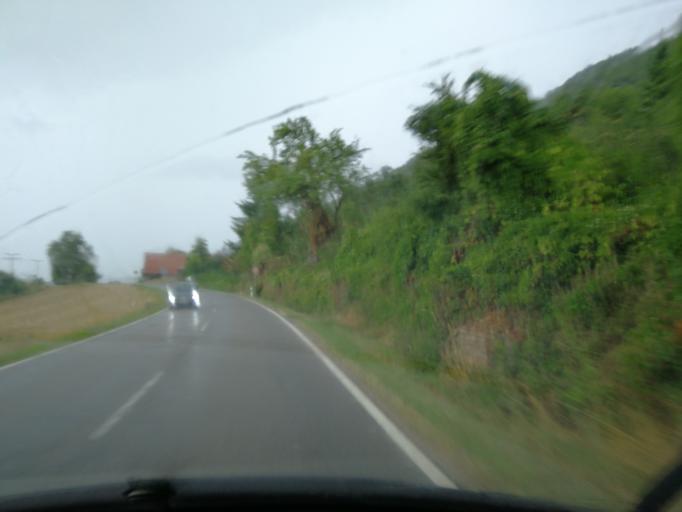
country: DE
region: Bavaria
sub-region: Upper Palatinate
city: Donaustauf
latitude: 49.0252
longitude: 12.2514
